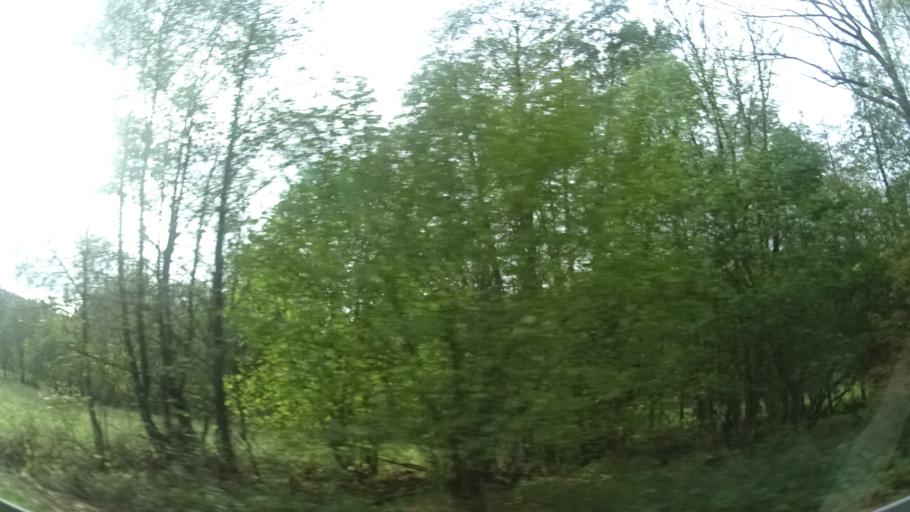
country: DE
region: Bavaria
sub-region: Regierungsbezirk Unterfranken
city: Aubstadt
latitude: 50.3469
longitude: 10.4146
